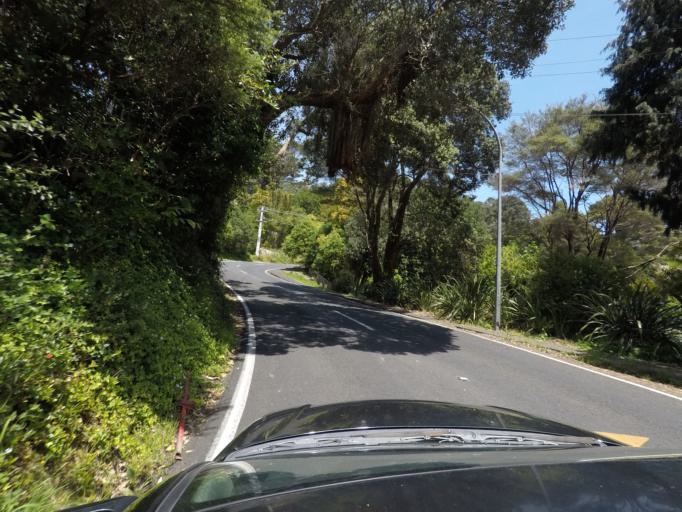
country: NZ
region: Auckland
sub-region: Auckland
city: Titirangi
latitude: -36.9683
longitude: 174.6402
